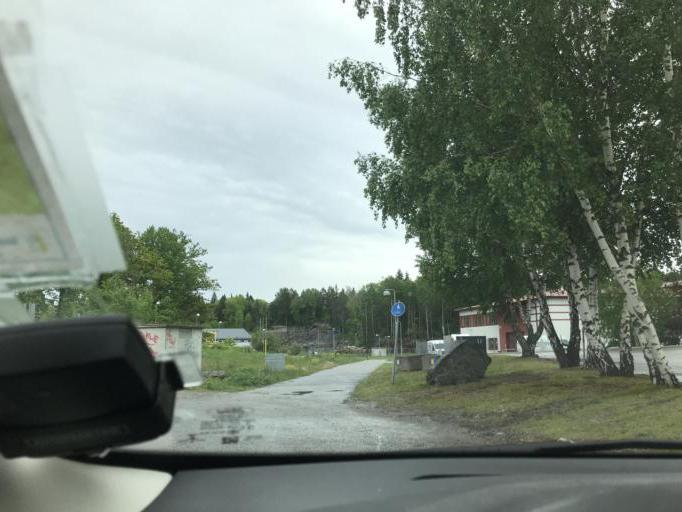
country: SE
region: Stockholm
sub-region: Huddinge Kommun
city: Segeltorp
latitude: 59.2668
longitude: 17.9275
